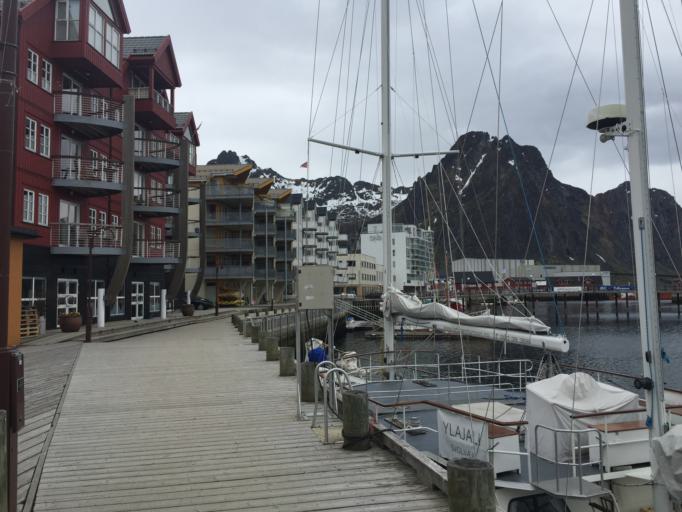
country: NO
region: Nordland
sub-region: Vagan
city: Svolvaer
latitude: 68.2327
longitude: 14.5667
